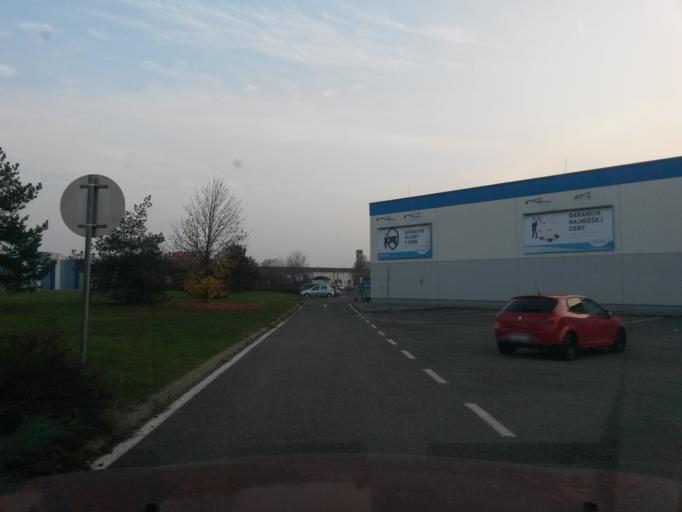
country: SK
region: Kosicky
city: Kosice
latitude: 48.6958
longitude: 21.2473
